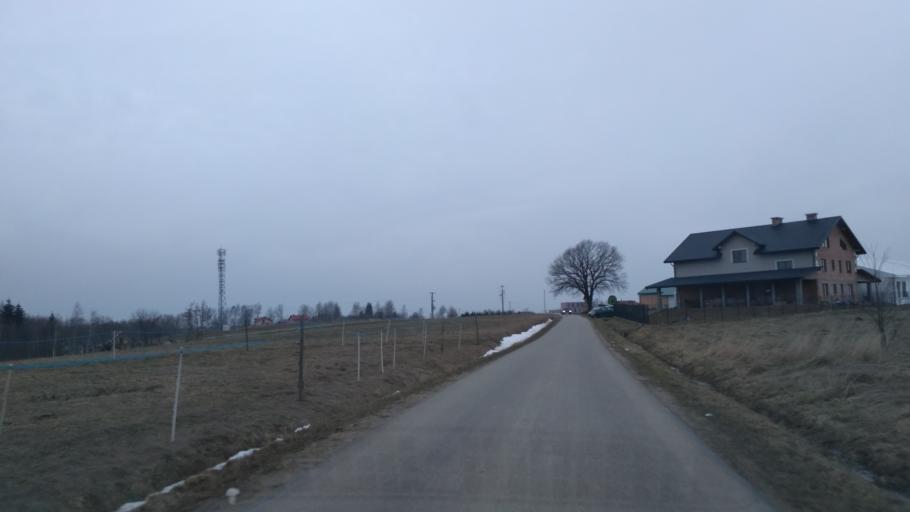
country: PL
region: Subcarpathian Voivodeship
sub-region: Powiat rzeszowski
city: Chmielnik
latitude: 49.9852
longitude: 22.1530
